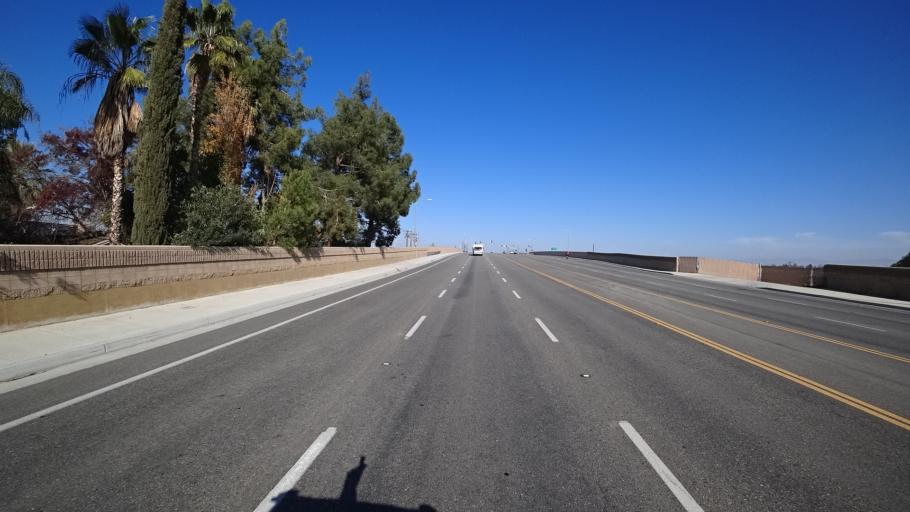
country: US
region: California
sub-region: Kern County
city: Rosedale
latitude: 35.3585
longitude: -119.1456
